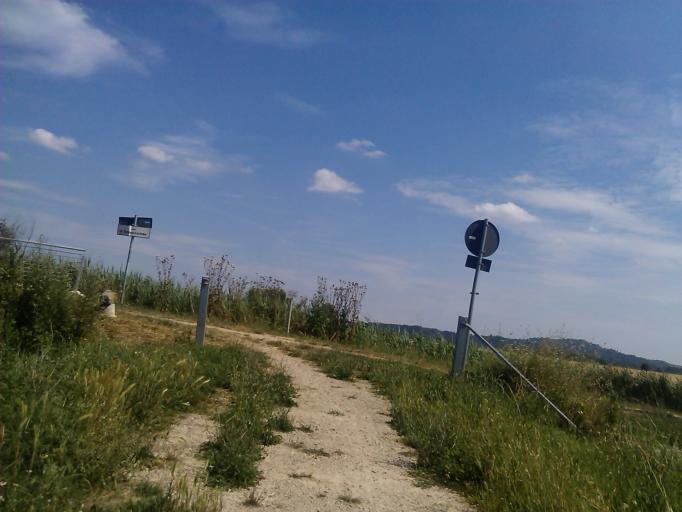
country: IT
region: Umbria
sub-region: Provincia di Perugia
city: Pozzuolo
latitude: 43.0733
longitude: 11.9242
